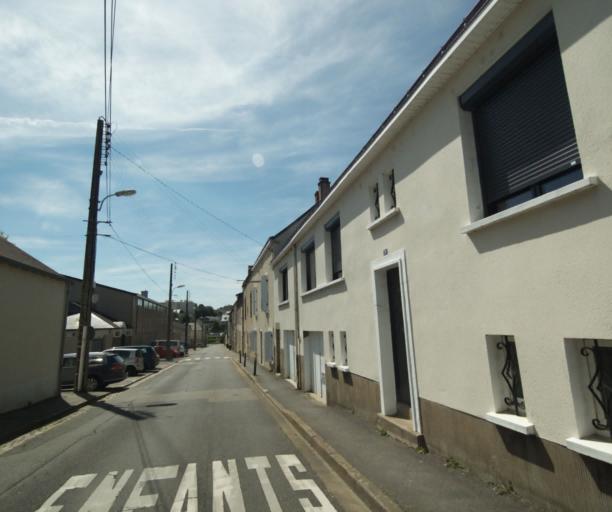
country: FR
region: Pays de la Loire
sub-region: Departement de la Mayenne
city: Laval
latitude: 48.0784
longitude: -0.7672
